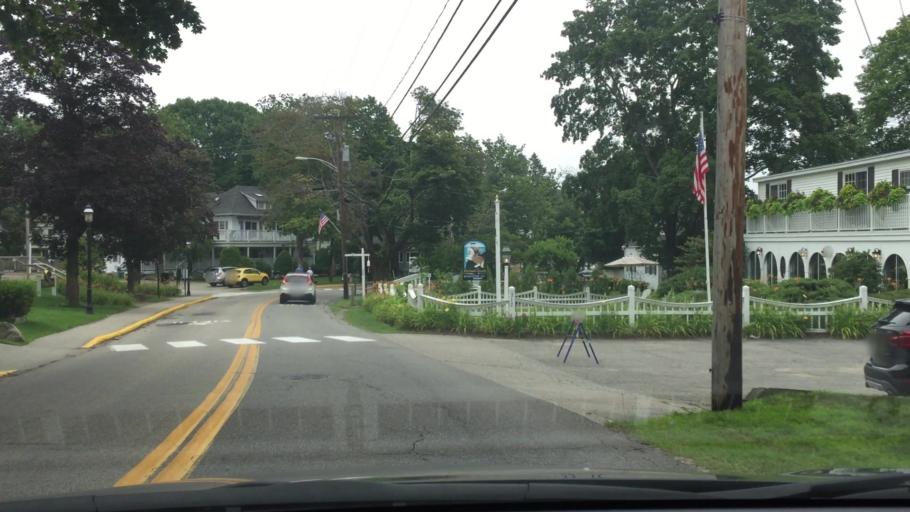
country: US
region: Maine
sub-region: York County
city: Ogunquit
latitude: 43.2396
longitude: -70.5953
